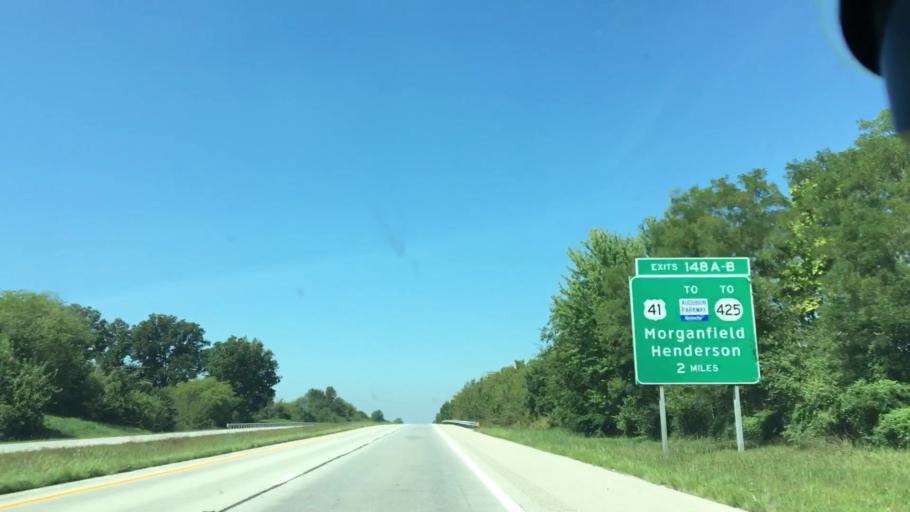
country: US
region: Kentucky
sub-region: Henderson County
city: Henderson
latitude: 37.7728
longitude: -87.5382
